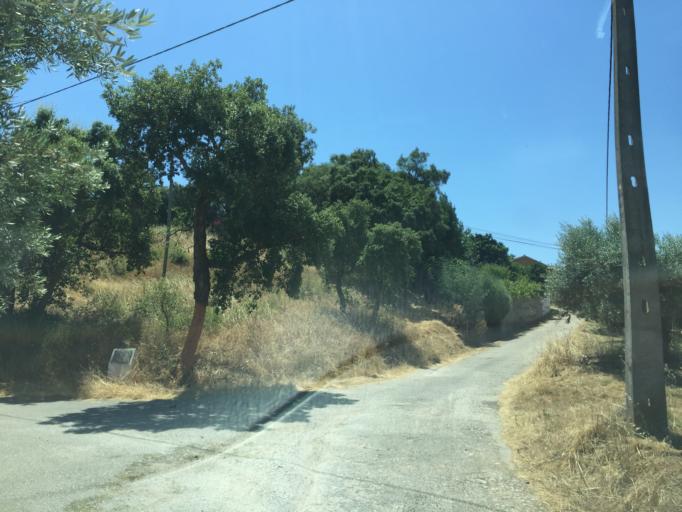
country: PT
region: Santarem
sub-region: Tomar
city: Tomar
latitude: 39.5956
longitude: -8.3521
